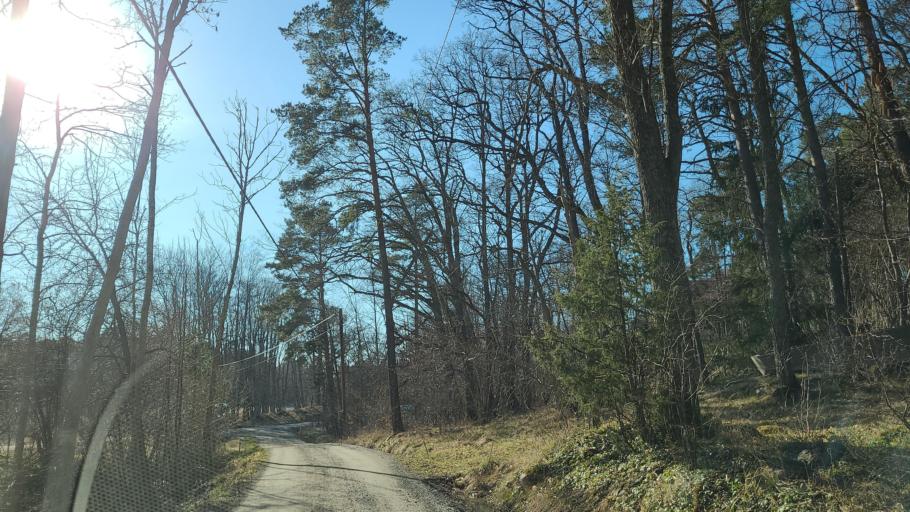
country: SE
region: Stockholm
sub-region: Varmdo Kommun
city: Holo
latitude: 59.3638
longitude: 18.6540
